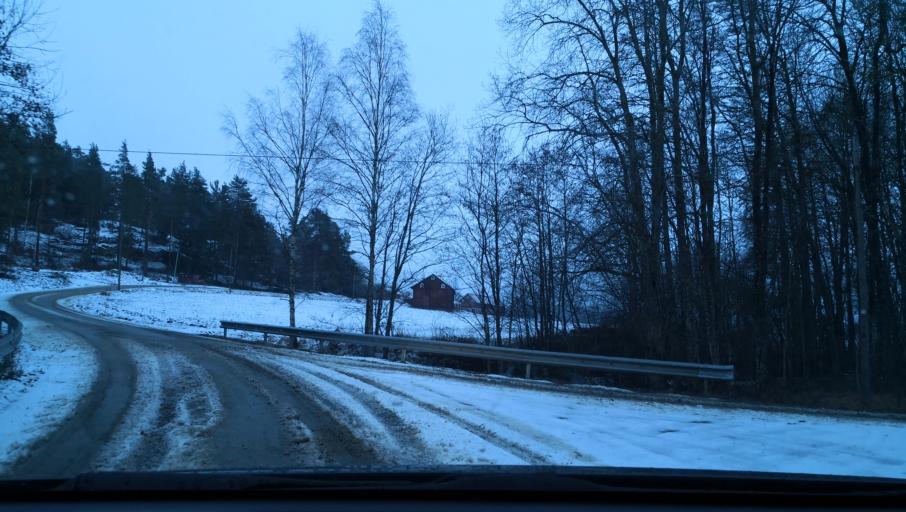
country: SE
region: Vaestmanland
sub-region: Kungsors Kommun
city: Kungsoer
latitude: 59.3960
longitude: 16.2072
